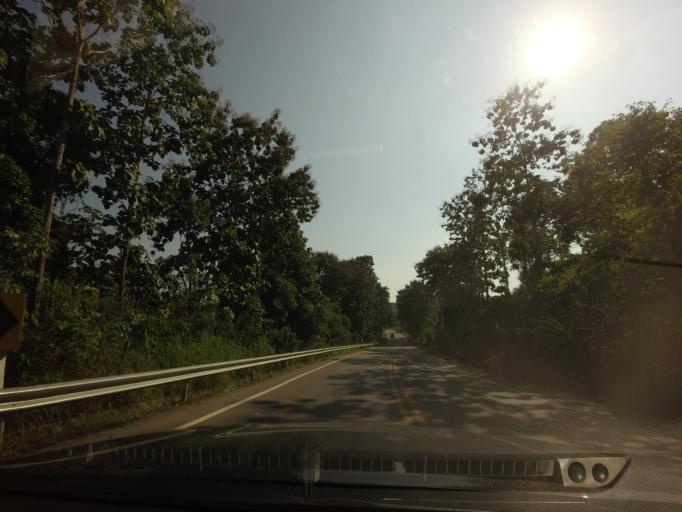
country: TH
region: Nan
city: Nan
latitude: 18.8337
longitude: 100.8101
